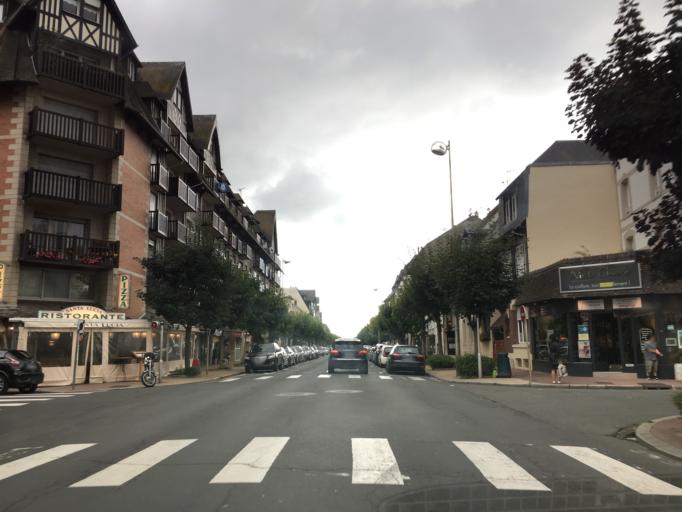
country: FR
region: Lower Normandy
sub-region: Departement du Calvados
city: Trouville-sur-Mer
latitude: 49.3596
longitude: 0.0800
